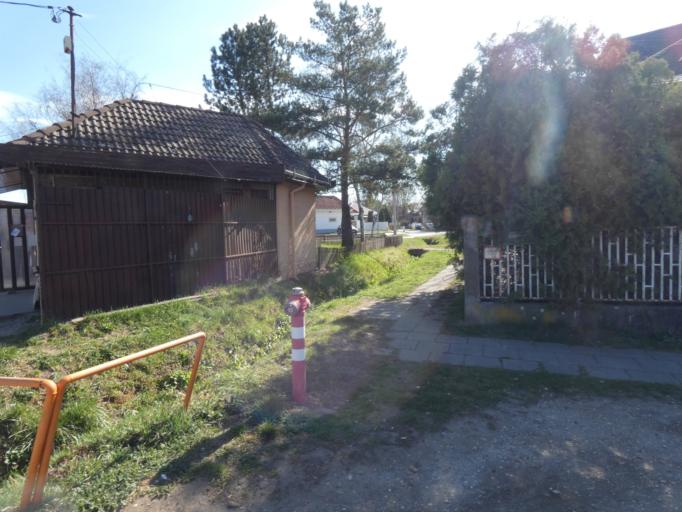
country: HU
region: Pest
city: Isaszeg
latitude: 47.5275
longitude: 19.3904
